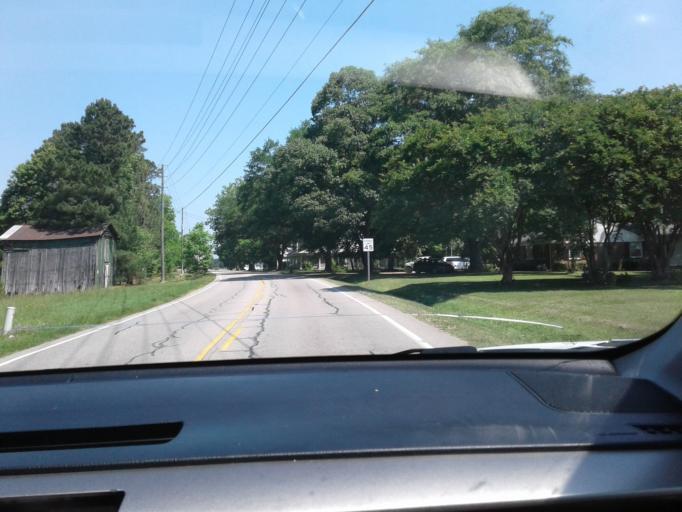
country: US
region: North Carolina
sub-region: Wake County
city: Fuquay-Varina
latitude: 35.5986
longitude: -78.8373
